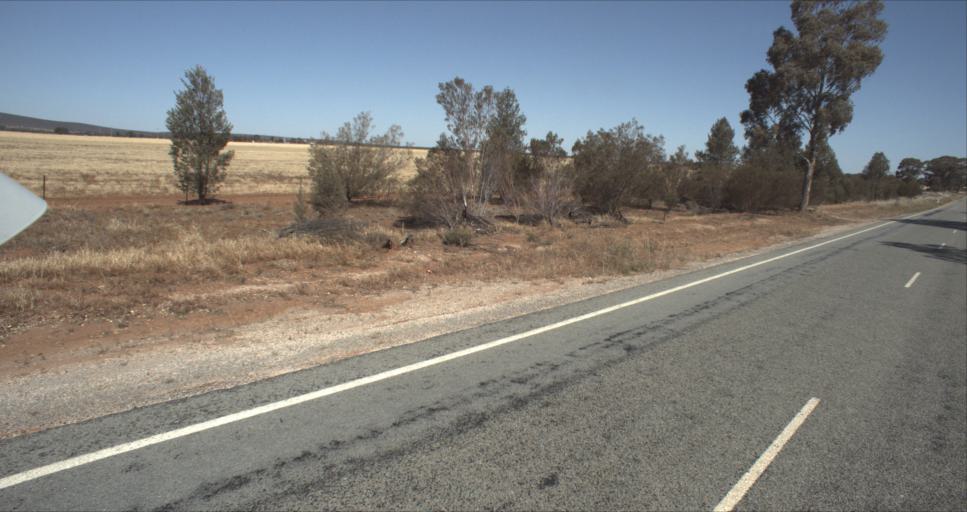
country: AU
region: New South Wales
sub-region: Leeton
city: Leeton
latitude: -34.4859
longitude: 146.4333
